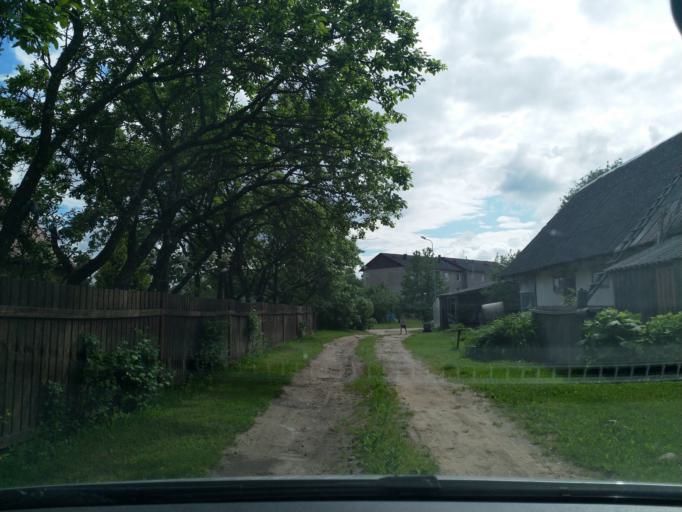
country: LV
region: Kuldigas Rajons
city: Kuldiga
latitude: 56.8438
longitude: 21.9468
